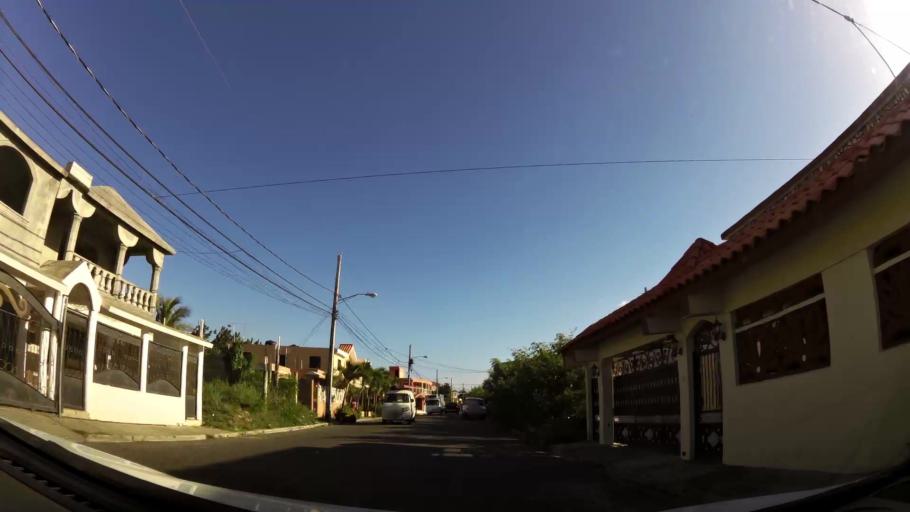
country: DO
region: Santo Domingo
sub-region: Santo Domingo
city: Santo Domingo Este
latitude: 18.4891
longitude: -69.8057
